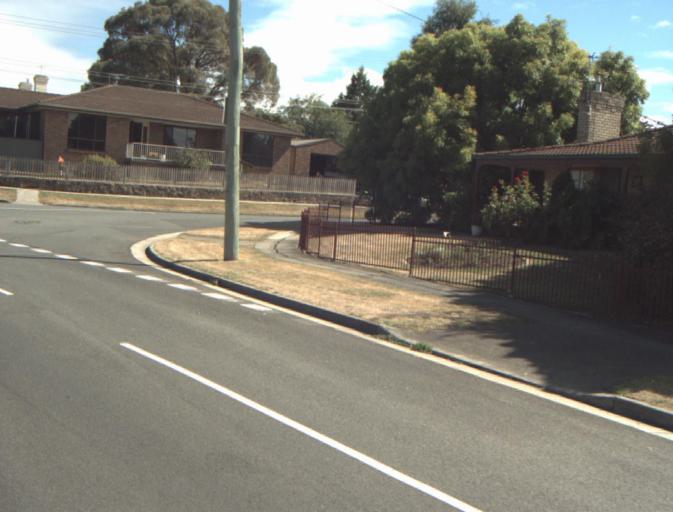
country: AU
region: Tasmania
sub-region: Launceston
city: Mayfield
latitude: -41.3878
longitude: 147.1171
